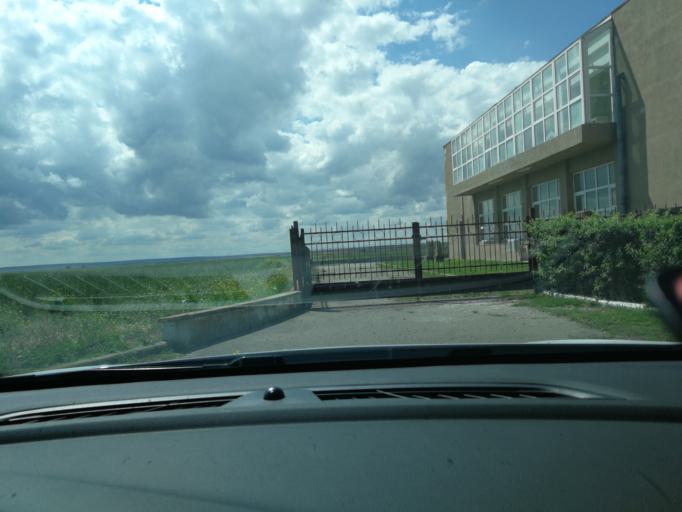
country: RO
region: Constanta
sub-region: Comuna Istria
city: Istria
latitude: 44.5458
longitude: 28.7703
